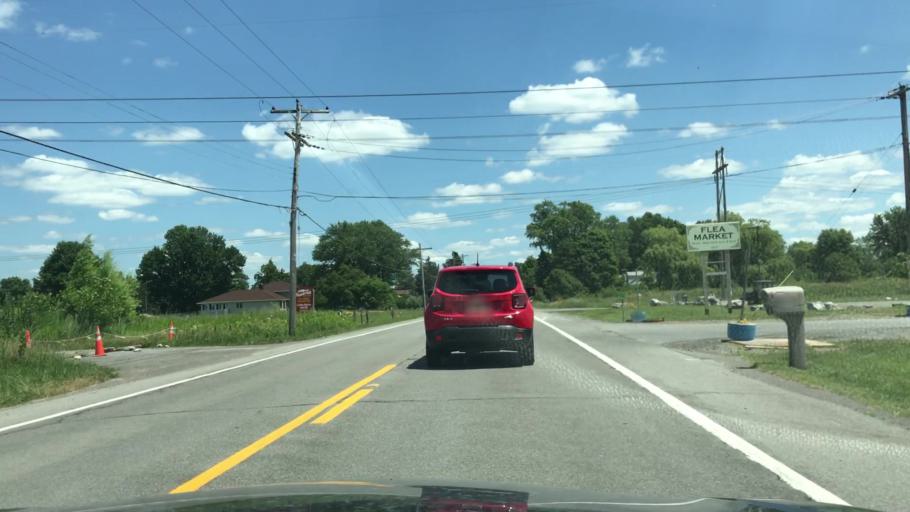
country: US
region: New York
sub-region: Erie County
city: East Aurora
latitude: 42.7674
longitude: -78.5698
